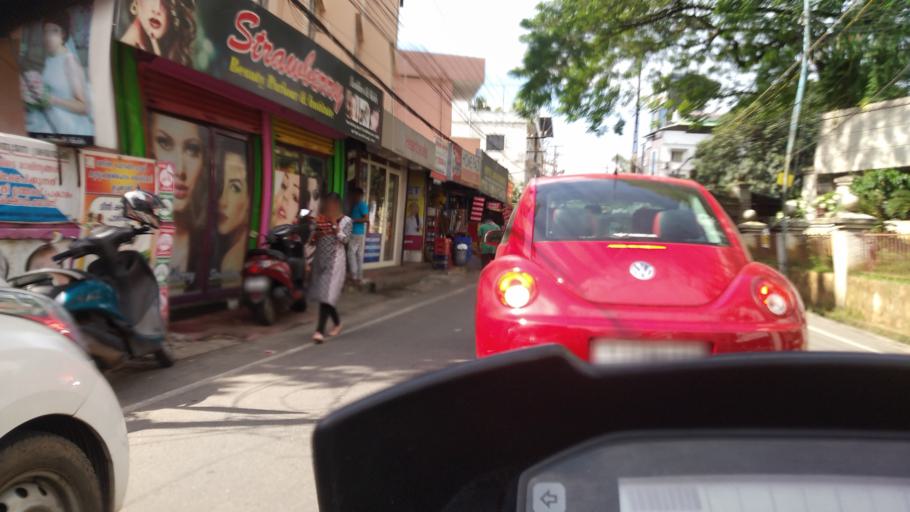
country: IN
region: Kerala
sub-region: Ernakulam
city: Cochin
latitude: 9.9917
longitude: 76.2876
